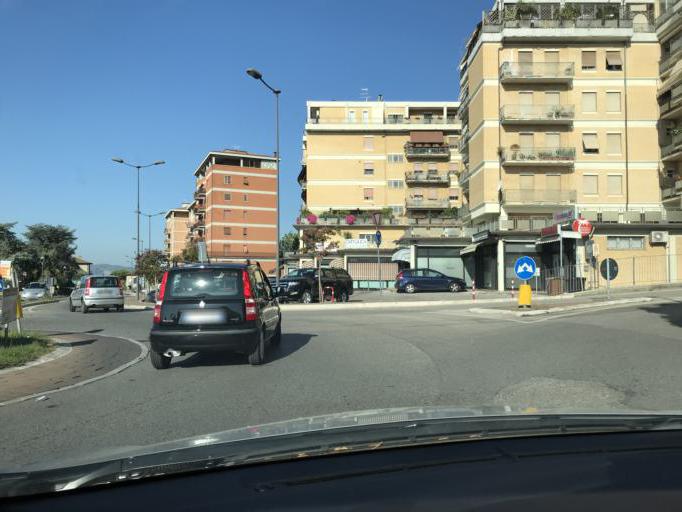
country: IT
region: Umbria
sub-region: Provincia di Perugia
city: Chiugiana-La Commenda
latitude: 43.1033
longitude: 12.3162
